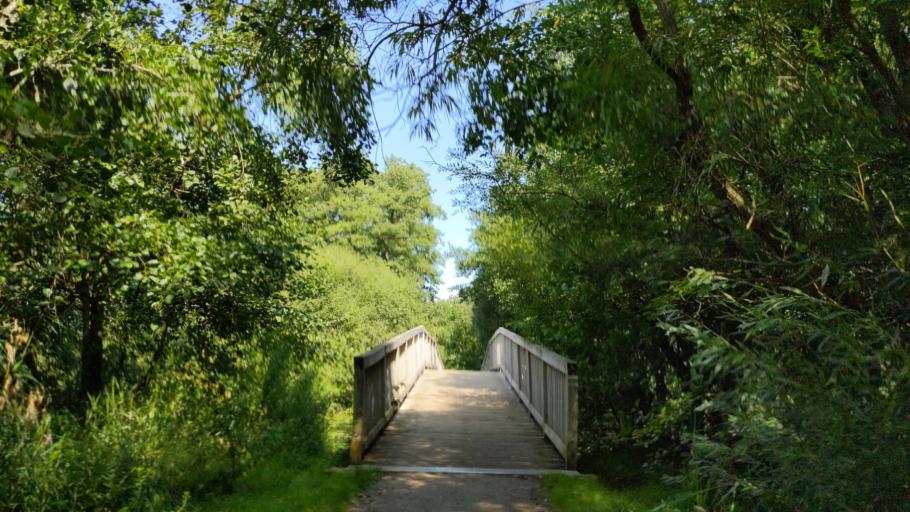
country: DE
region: Schleswig-Holstein
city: Eutin
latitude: 54.1491
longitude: 10.6149
